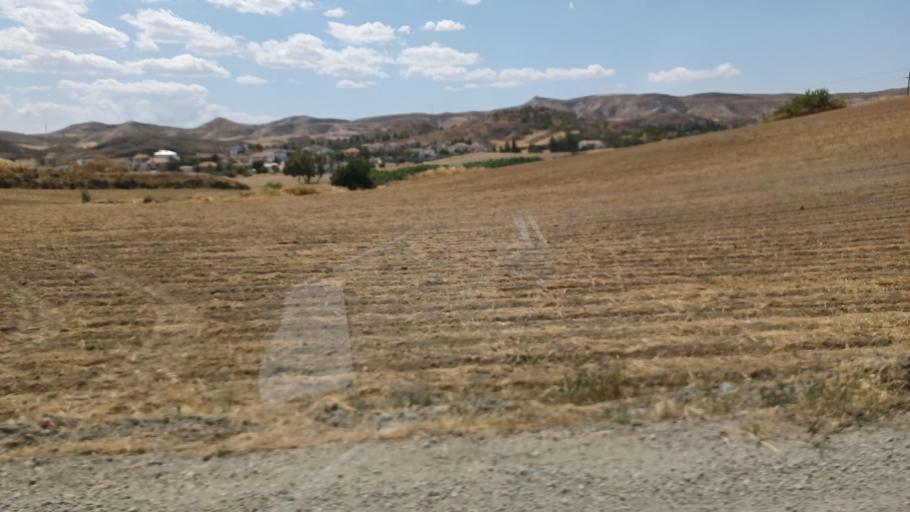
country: CY
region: Larnaka
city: Troulloi
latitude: 35.0070
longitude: 33.5759
